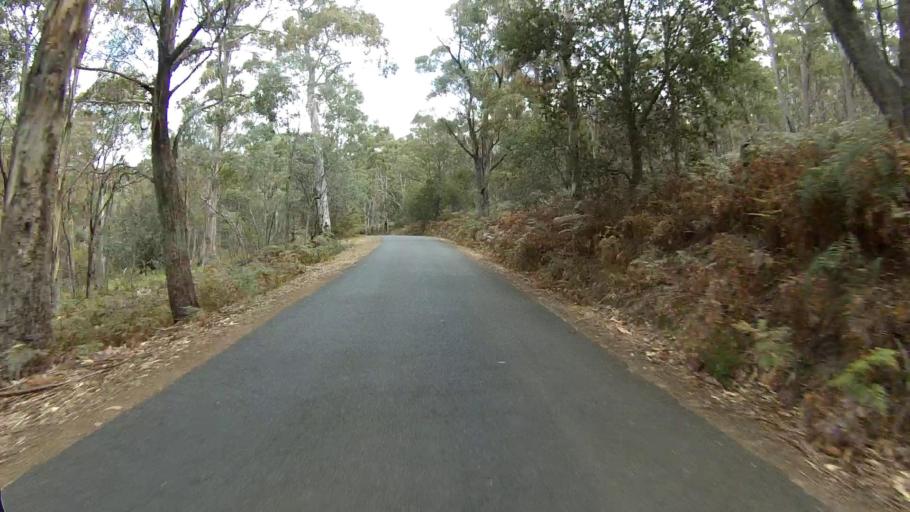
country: AU
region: Tasmania
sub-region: Sorell
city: Sorell
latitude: -42.6021
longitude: 147.9227
